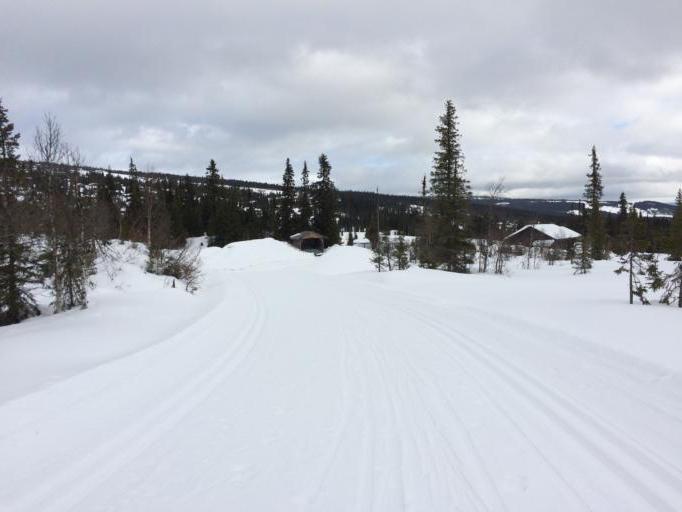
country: NO
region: Oppland
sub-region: Gausdal
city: Segalstad bru
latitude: 61.3286
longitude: 10.1027
